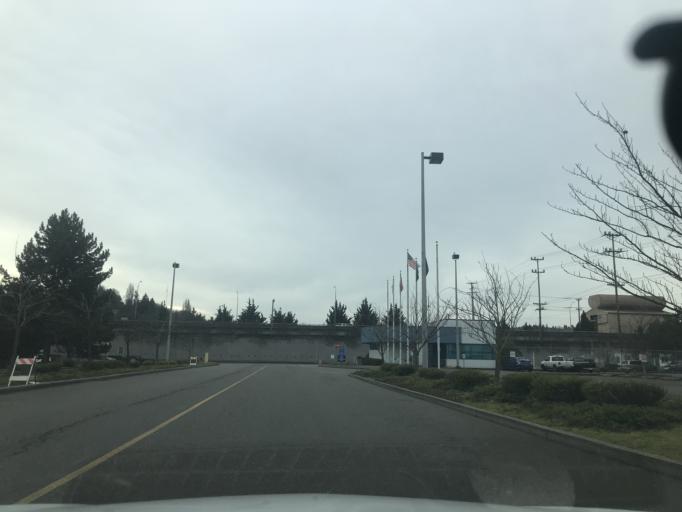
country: US
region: Washington
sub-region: King County
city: Seattle
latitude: 47.5729
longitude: -122.3640
